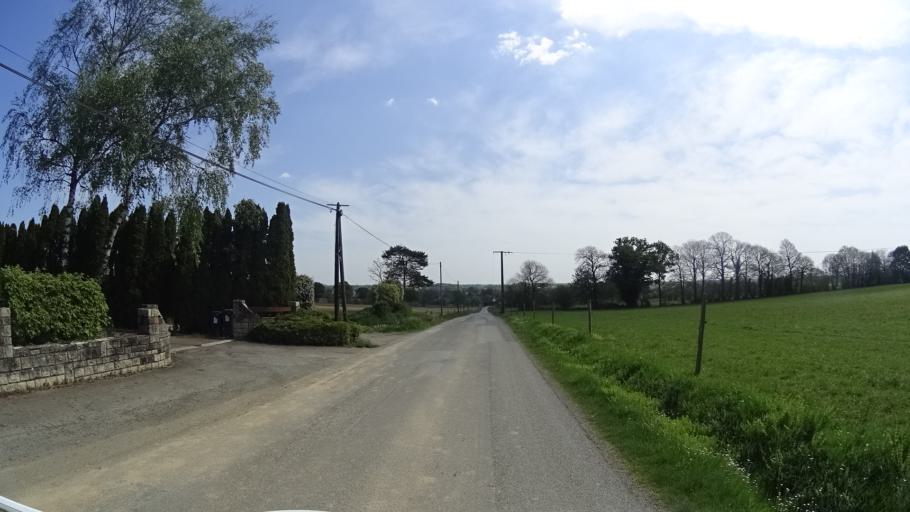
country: FR
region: Brittany
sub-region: Departement d'Ille-et-Vilaine
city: Torce
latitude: 48.0377
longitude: -1.2757
